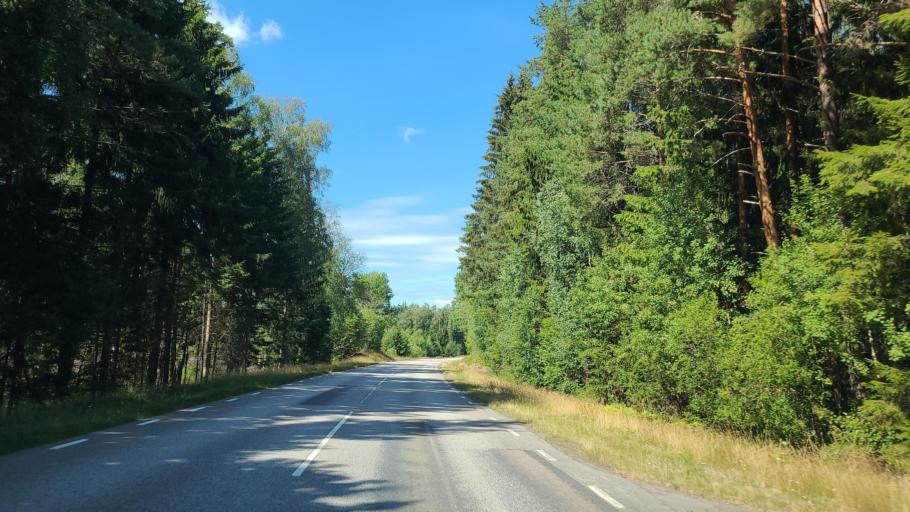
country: SE
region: Kalmar
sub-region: Nybro Kommun
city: Nybro
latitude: 56.5631
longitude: 15.8154
